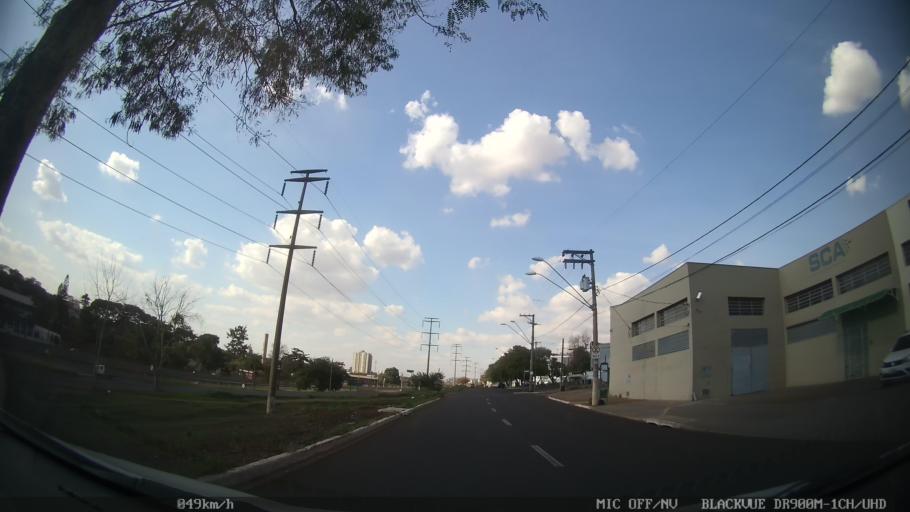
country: BR
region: Sao Paulo
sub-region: Ribeirao Preto
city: Ribeirao Preto
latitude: -21.1798
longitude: -47.8385
